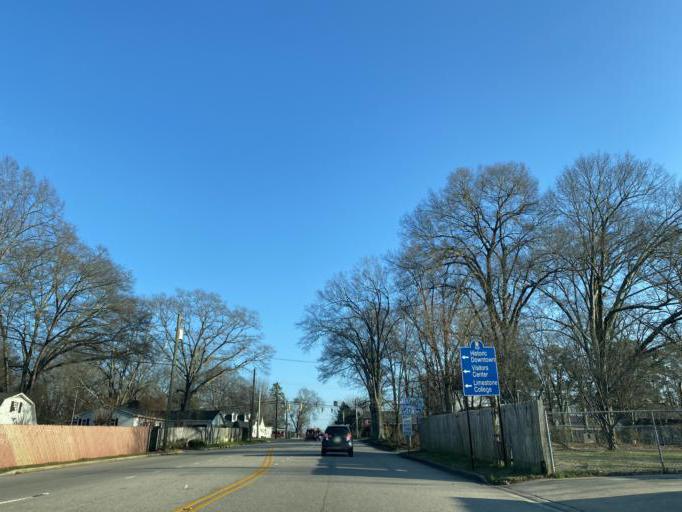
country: US
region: South Carolina
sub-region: Cherokee County
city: Gaffney
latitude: 35.0631
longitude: -81.6594
